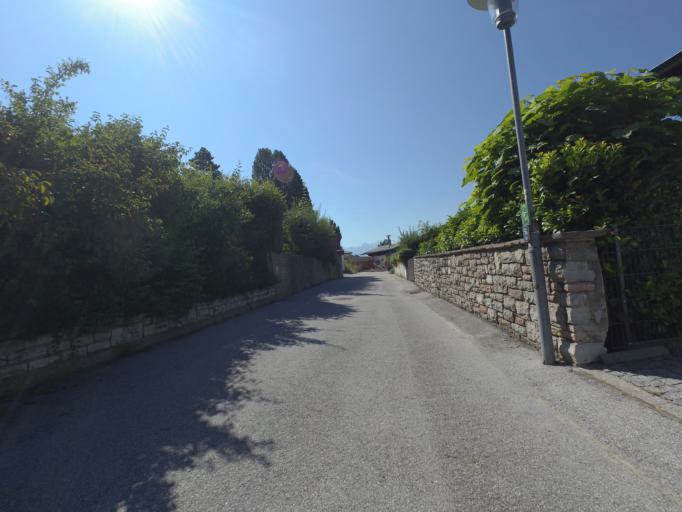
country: AT
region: Salzburg
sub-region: Politischer Bezirk Hallein
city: Hallein
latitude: 47.6913
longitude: 13.1145
